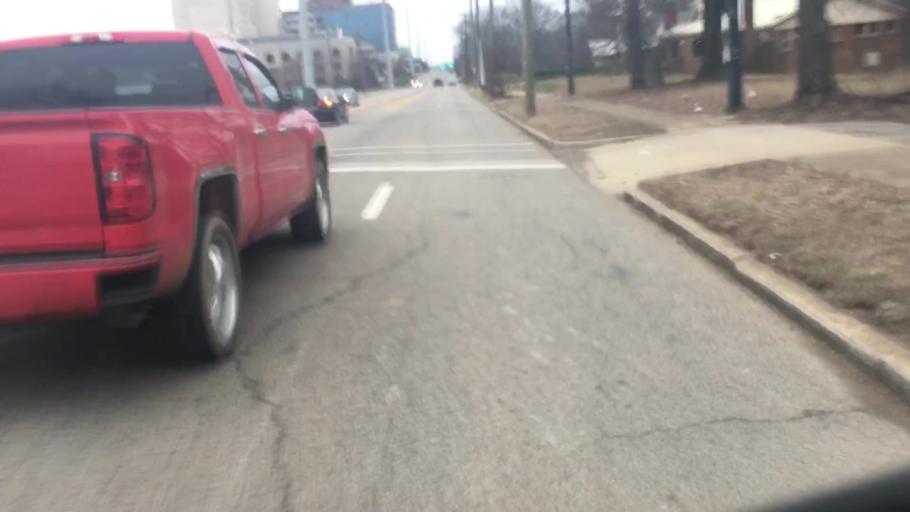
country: US
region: Alabama
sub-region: Jefferson County
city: Birmingham
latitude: 33.5331
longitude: -86.8073
